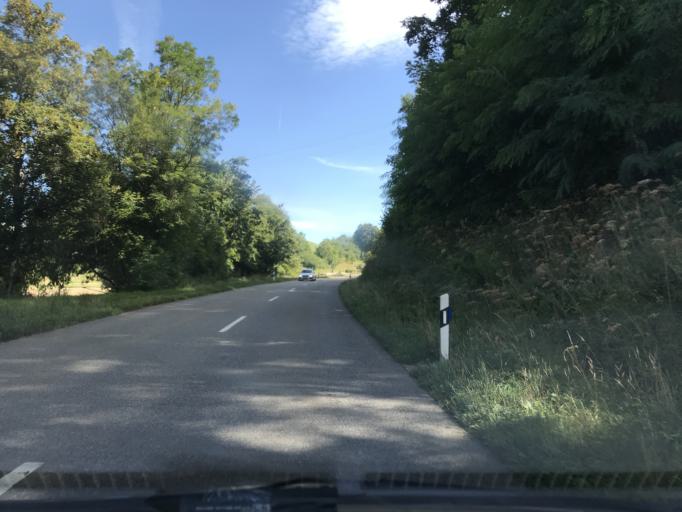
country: DE
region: Baden-Wuerttemberg
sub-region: Freiburg Region
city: Schopfheim
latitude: 47.6411
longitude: 7.8367
